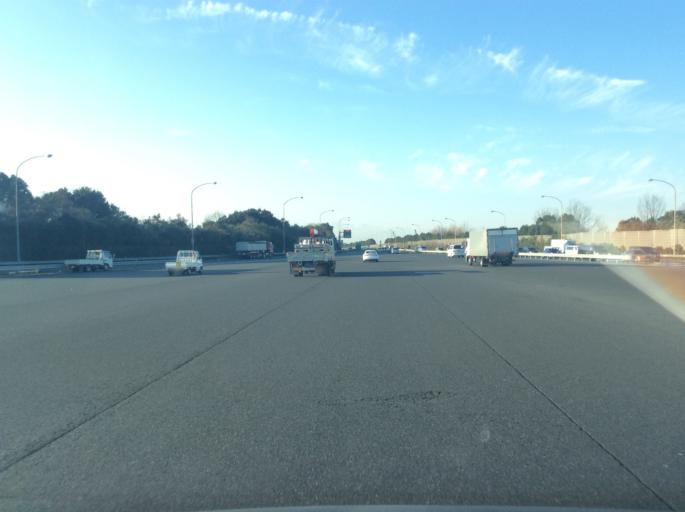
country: JP
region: Chiba
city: Nagareyama
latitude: 35.8650
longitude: 139.8829
